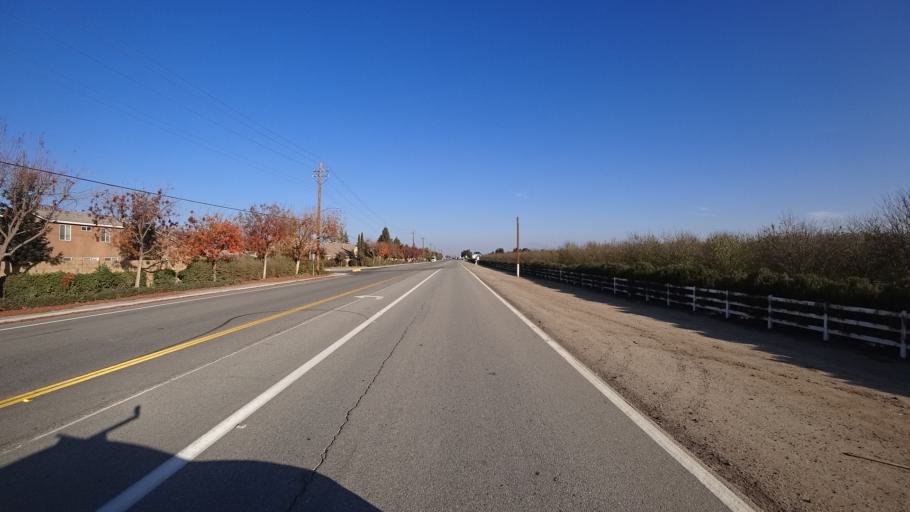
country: US
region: California
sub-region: Kern County
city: Rosedale
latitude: 35.2963
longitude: -119.1350
